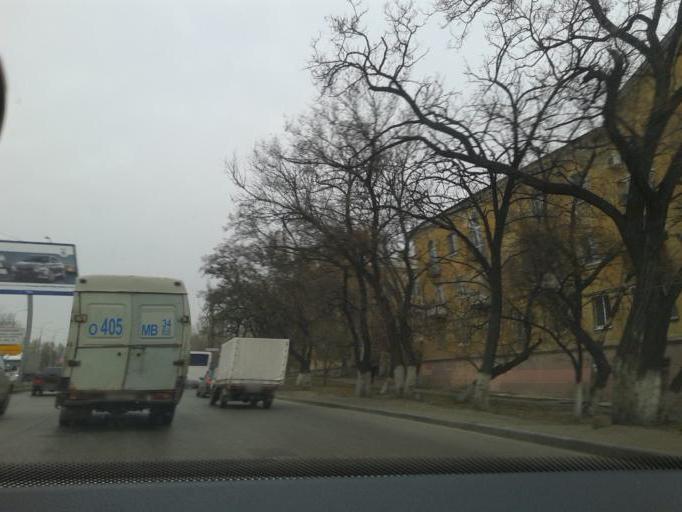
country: RU
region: Volgograd
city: Volgograd
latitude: 48.6565
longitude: 44.4374
